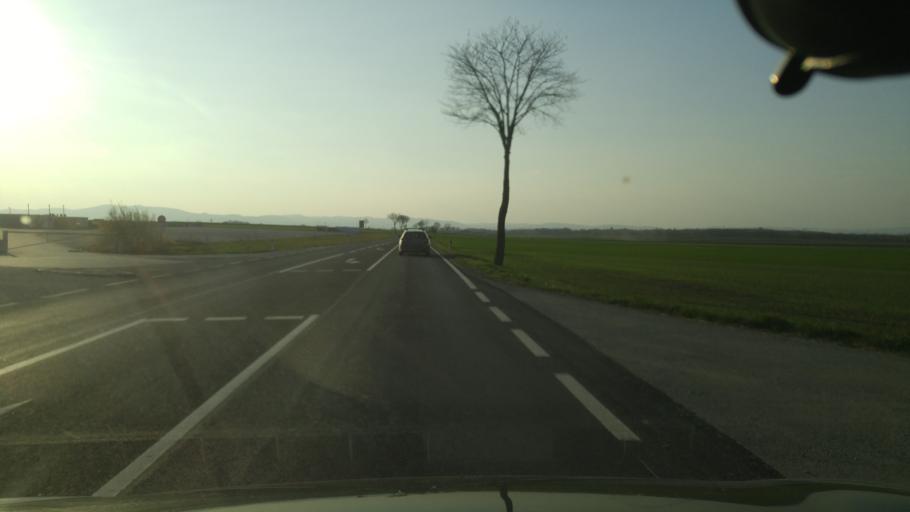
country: AT
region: Lower Austria
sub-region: Politischer Bezirk Wien-Umgebung
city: Gramatneusiedl
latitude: 48.0398
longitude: 16.4718
